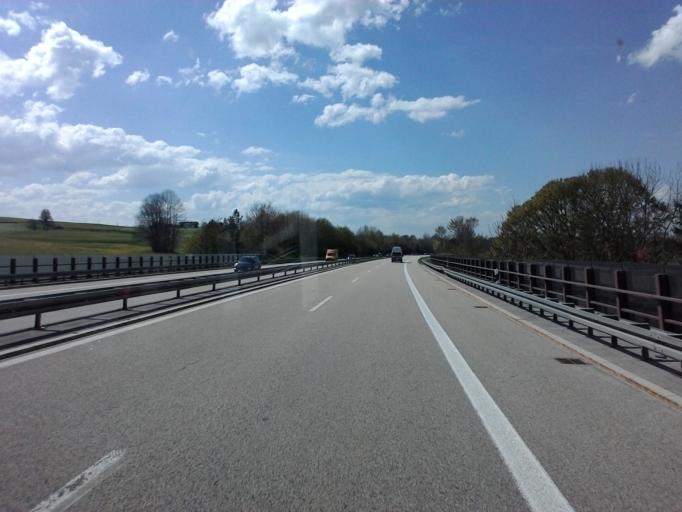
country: DE
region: Bavaria
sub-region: Swabia
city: Nesselwang
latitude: 47.6416
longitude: 10.5019
